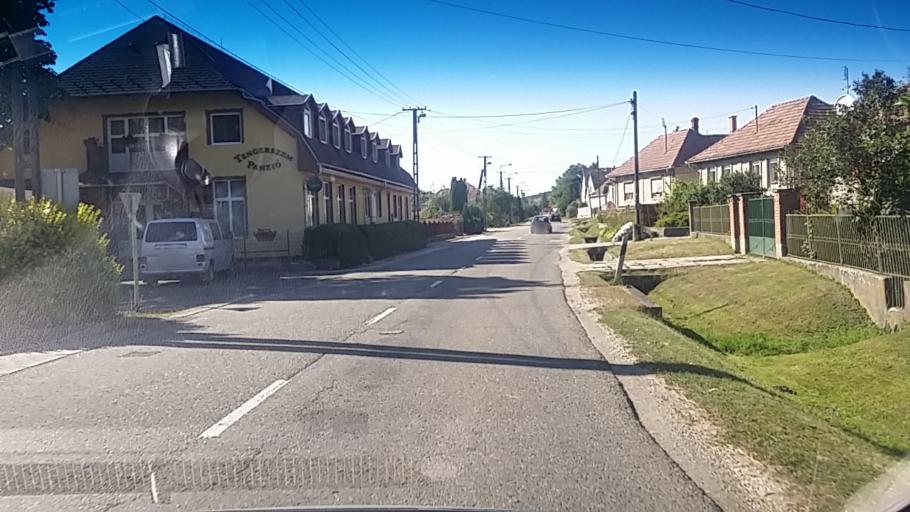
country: HU
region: Nograd
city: Retsag
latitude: 47.9264
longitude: 19.1733
